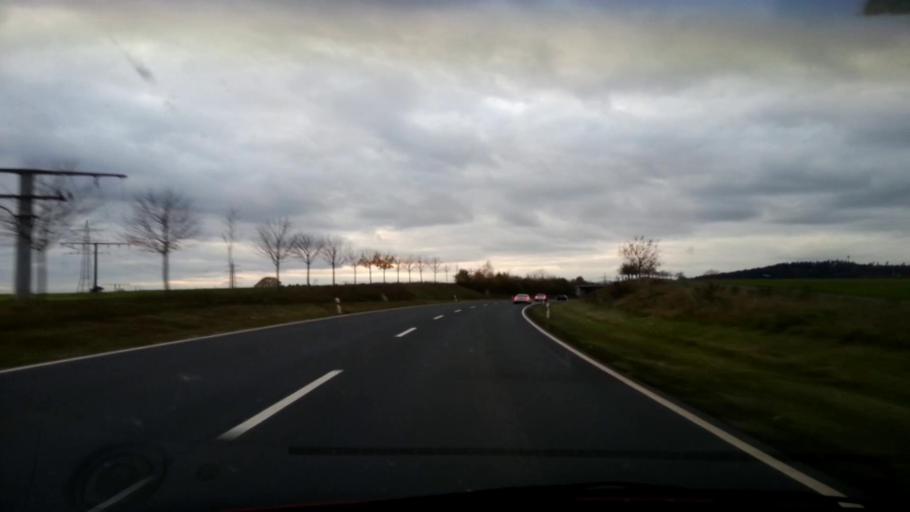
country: DE
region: Bavaria
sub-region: Upper Franconia
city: Sonnefeld
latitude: 50.2131
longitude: 11.1292
